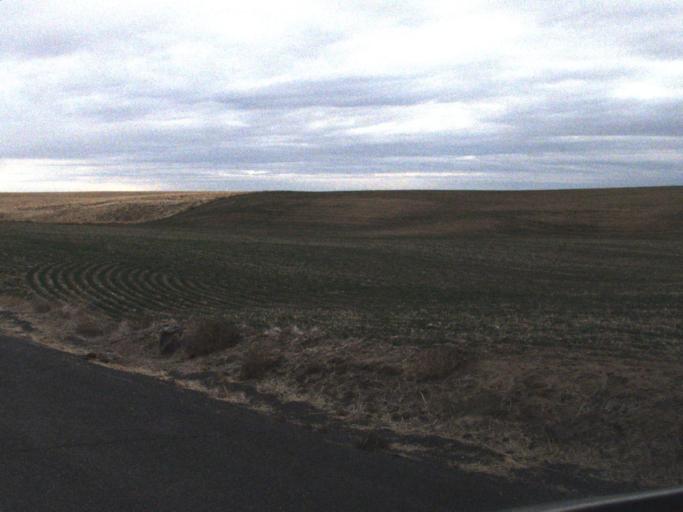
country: US
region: Washington
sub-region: Adams County
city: Ritzville
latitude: 46.7952
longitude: -118.4290
